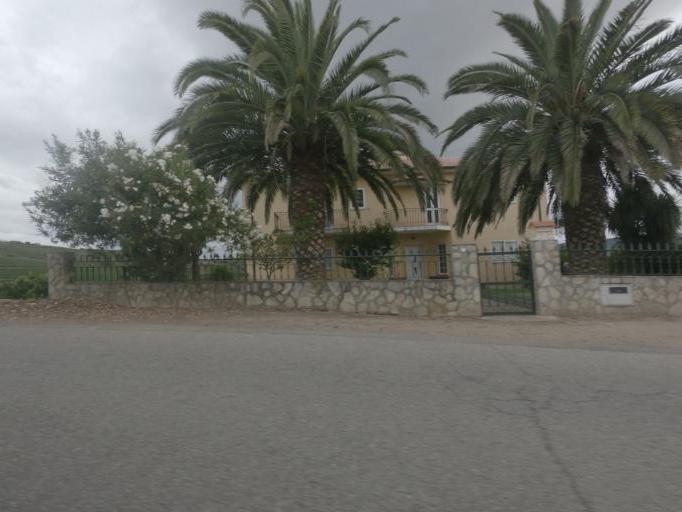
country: PT
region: Vila Real
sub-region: Sabrosa
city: Sabrosa
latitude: 41.2790
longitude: -7.5372
